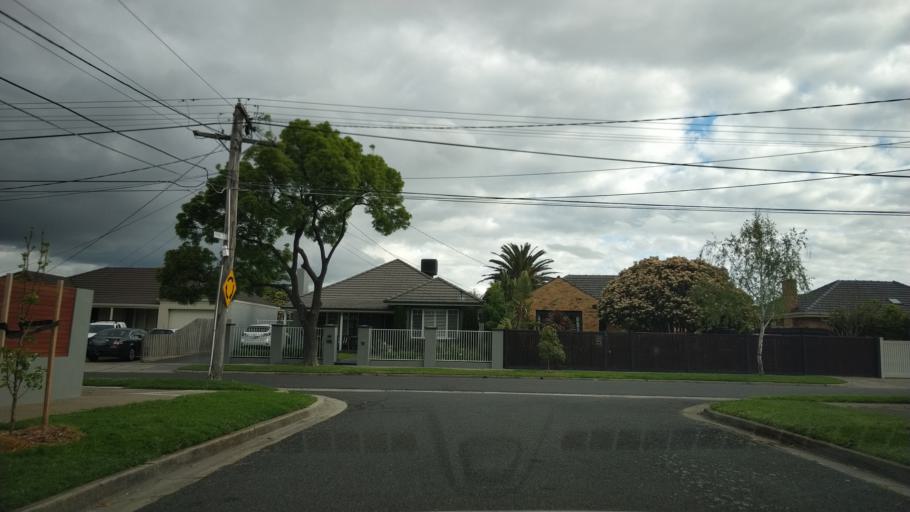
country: AU
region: Victoria
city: Highett
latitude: -37.9525
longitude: 145.0643
